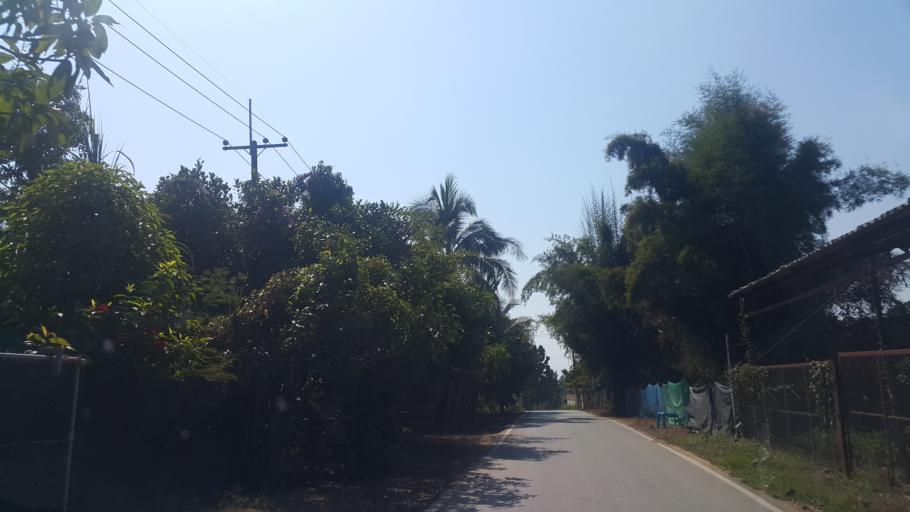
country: TH
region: Chiang Mai
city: San Kamphaeng
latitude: 18.7189
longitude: 99.1741
